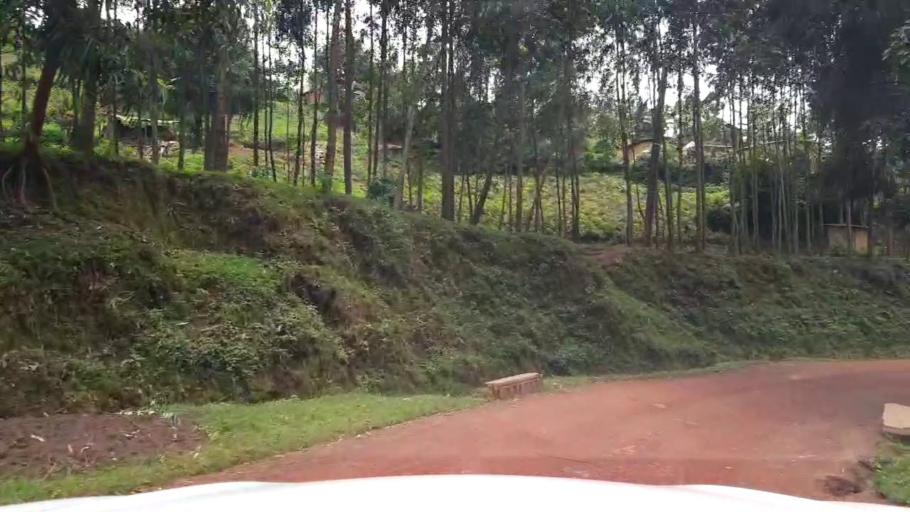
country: UG
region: Western Region
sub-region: Kisoro District
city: Kisoro
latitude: -1.4174
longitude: 29.8303
